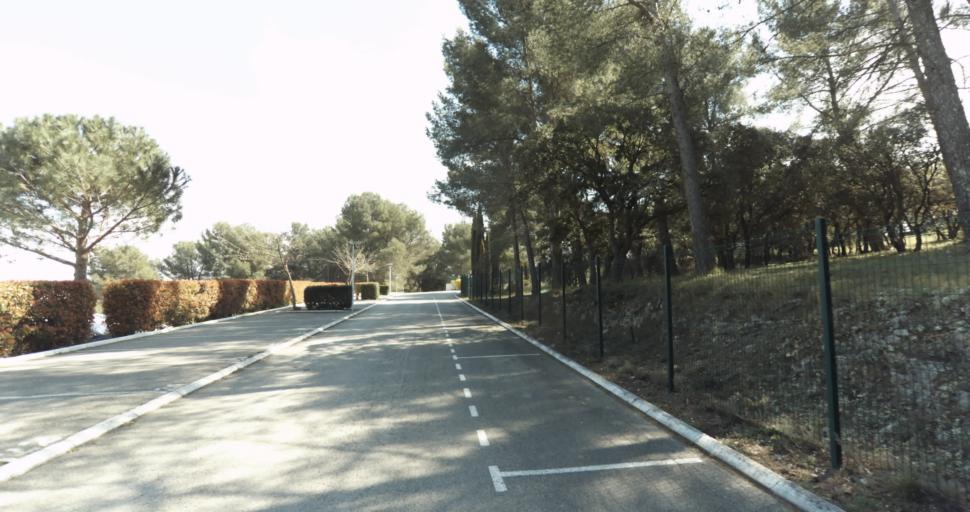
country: FR
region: Provence-Alpes-Cote d'Azur
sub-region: Departement des Bouches-du-Rhone
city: Cabries
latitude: 43.4815
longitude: 5.3626
